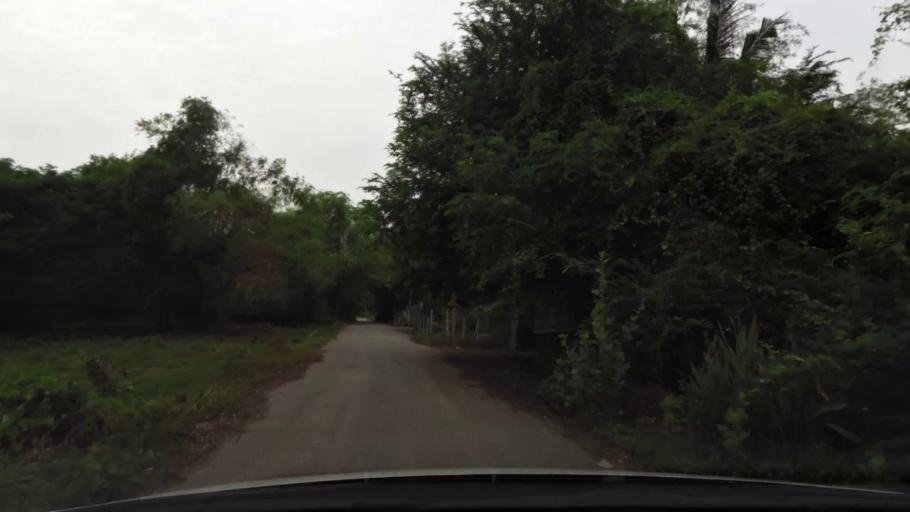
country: TH
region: Samut Sakhon
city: Ban Phaeo
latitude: 13.6057
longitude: 100.0086
